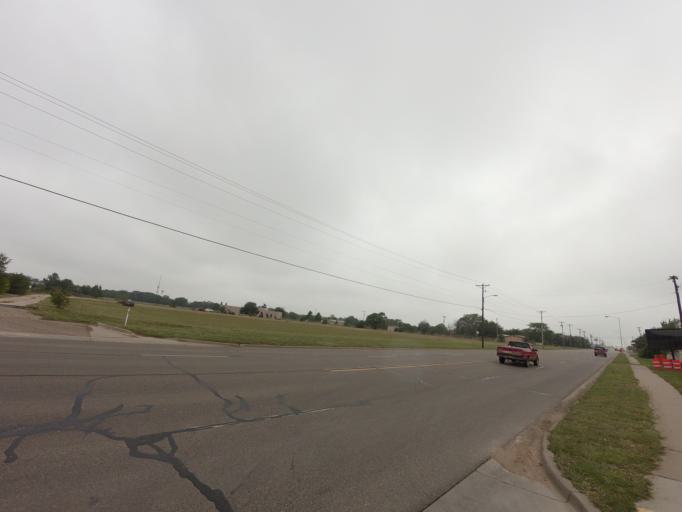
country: US
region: New Mexico
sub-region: Curry County
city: Clovis
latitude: 34.4340
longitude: -103.1906
